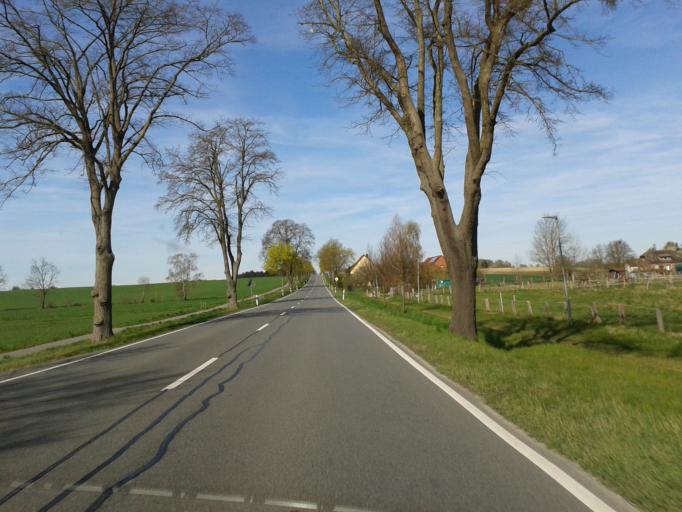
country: DE
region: Lower Saxony
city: Suhlendorf
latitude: 52.9492
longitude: 10.7212
